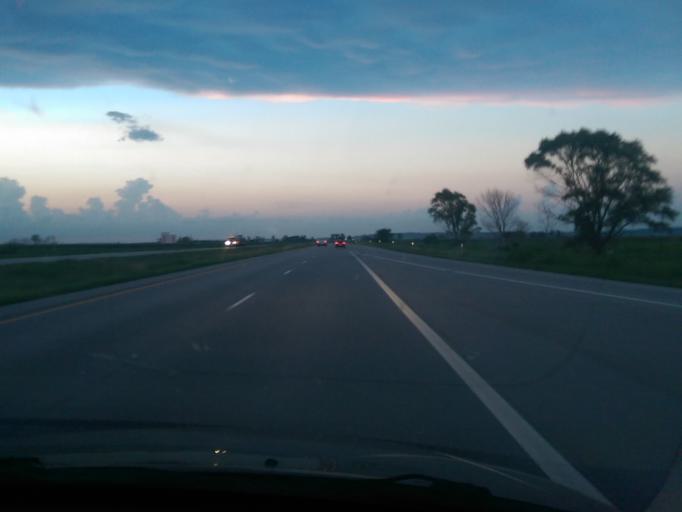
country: US
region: Nebraska
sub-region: Otoe County
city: Nebraska City
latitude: 40.7616
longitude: -95.8157
